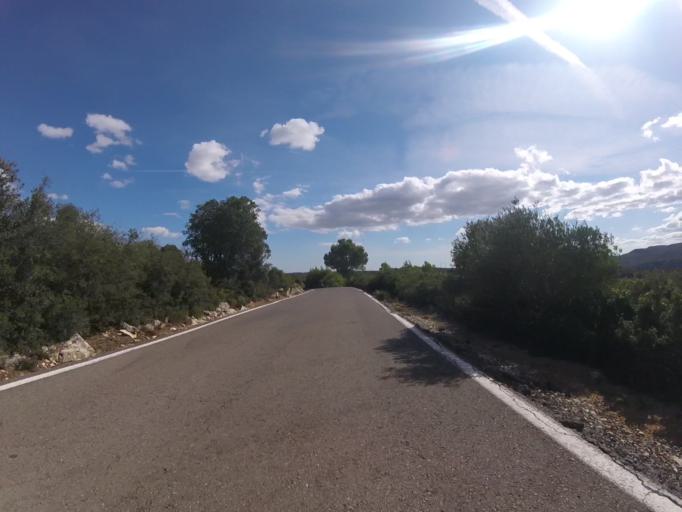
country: ES
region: Valencia
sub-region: Provincia de Castello
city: Albocasser
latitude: 40.3966
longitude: 0.0895
